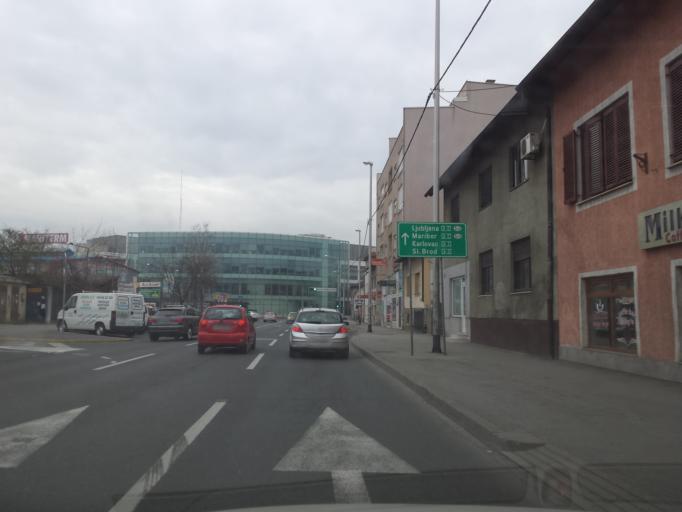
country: HR
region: Grad Zagreb
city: Jankomir
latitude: 45.8132
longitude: 15.9313
